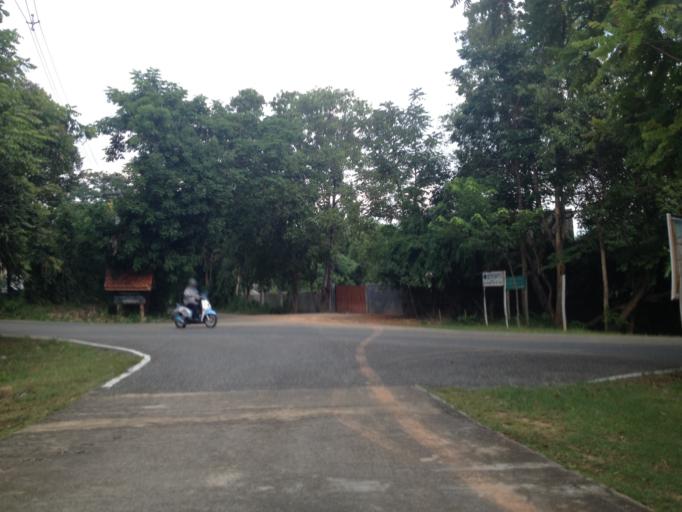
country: TH
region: Chiang Mai
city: Hang Dong
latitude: 18.7318
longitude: 98.9165
